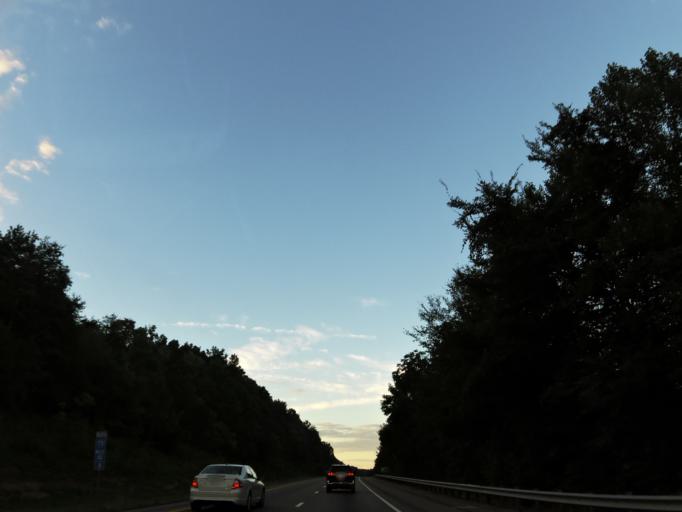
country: US
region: Tennessee
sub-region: Meigs County
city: Decatur
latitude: 35.3750
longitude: -84.7327
